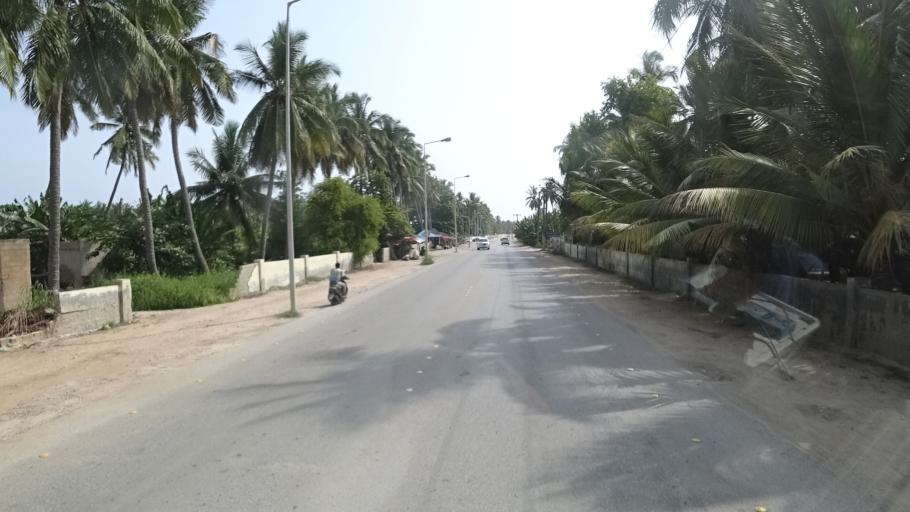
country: OM
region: Zufar
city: Salalah
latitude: 17.0164
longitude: 54.1542
